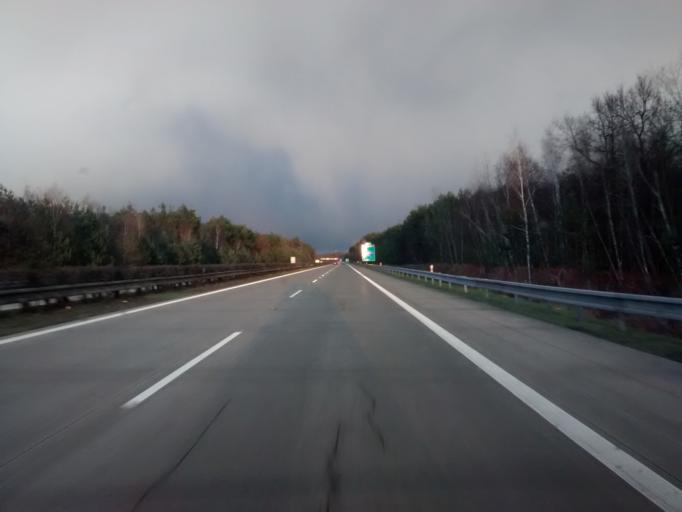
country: CZ
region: Central Bohemia
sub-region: Okres Nymburk
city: Podebrady
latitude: 50.1195
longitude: 15.1091
